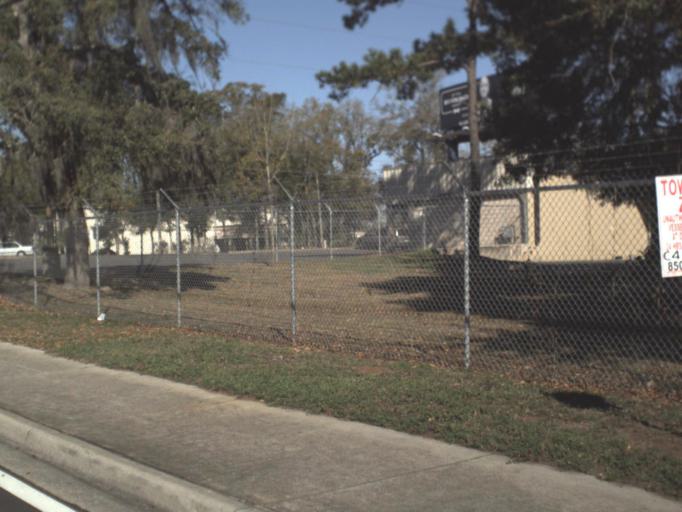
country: US
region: Florida
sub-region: Leon County
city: Tallahassee
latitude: 30.4054
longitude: -84.2799
